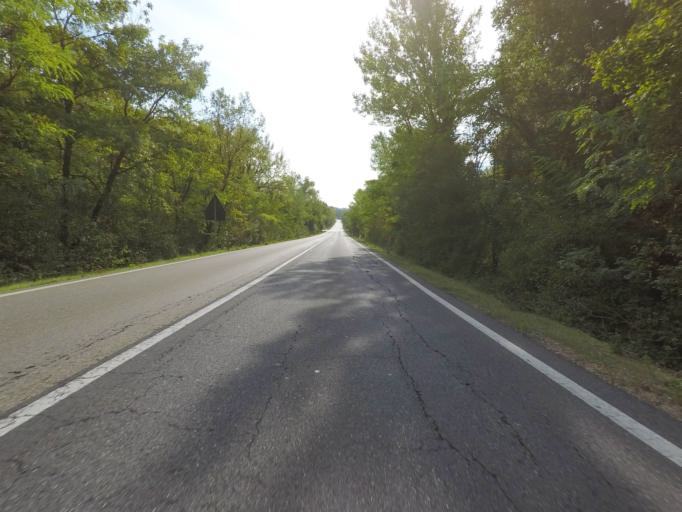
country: IT
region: Tuscany
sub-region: Provincia di Siena
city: Rosia
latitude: 43.1772
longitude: 11.2782
